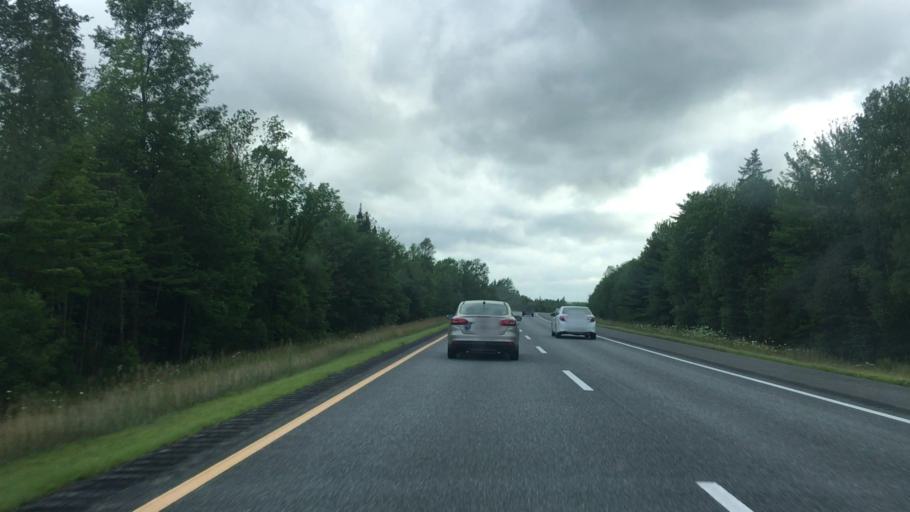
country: US
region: Maine
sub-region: Kennebec County
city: Clinton
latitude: 44.6686
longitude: -69.4898
